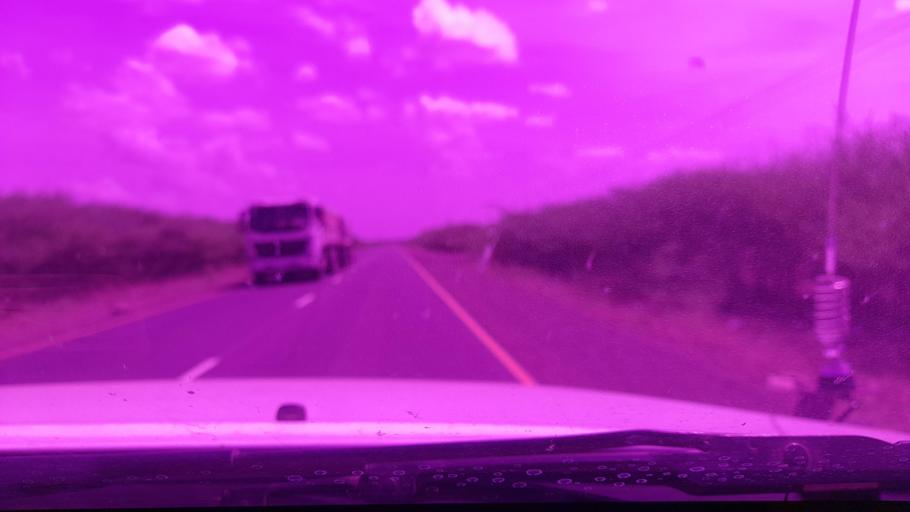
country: ET
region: Afar
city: Awash
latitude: 9.3589
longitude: 40.3053
